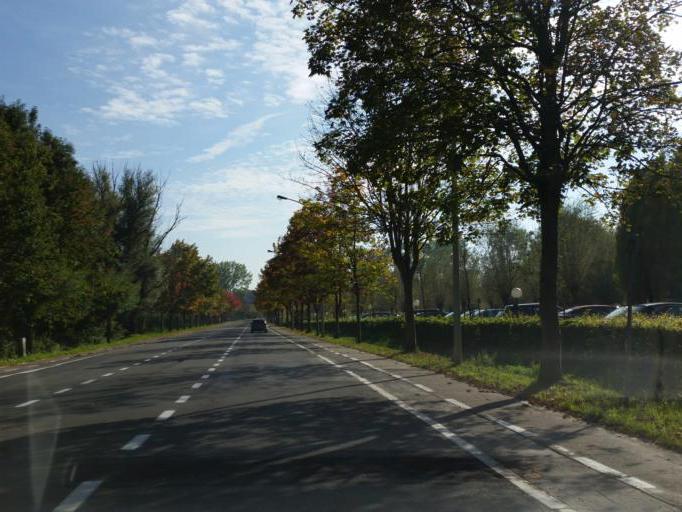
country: BE
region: Flanders
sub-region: Provincie Antwerpen
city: Aartselaar
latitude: 51.1490
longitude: 4.4043
